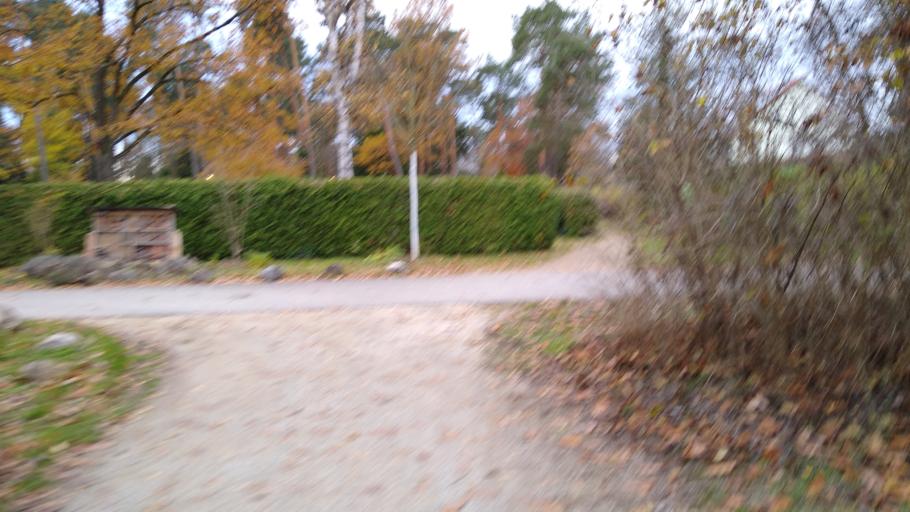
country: DE
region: Bavaria
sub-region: Regierungsbezirk Mittelfranken
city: Schwabach
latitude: 49.3376
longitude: 11.0384
